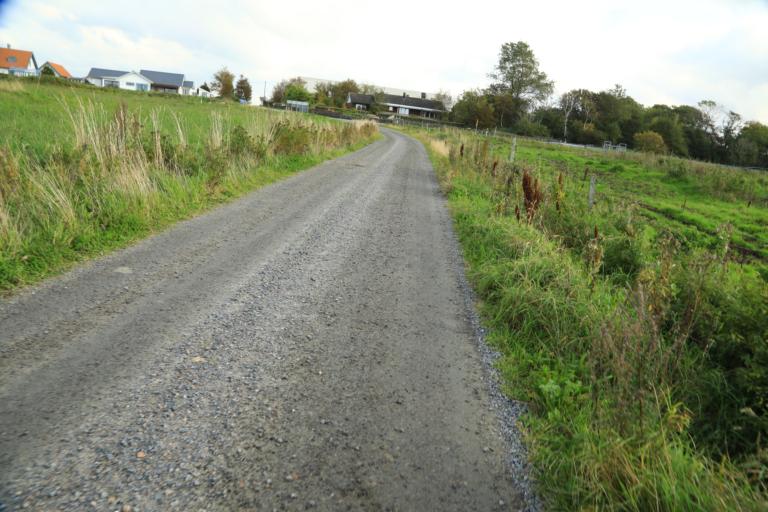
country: SE
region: Halland
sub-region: Varbergs Kommun
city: Traslovslage
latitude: 57.0272
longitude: 12.3323
